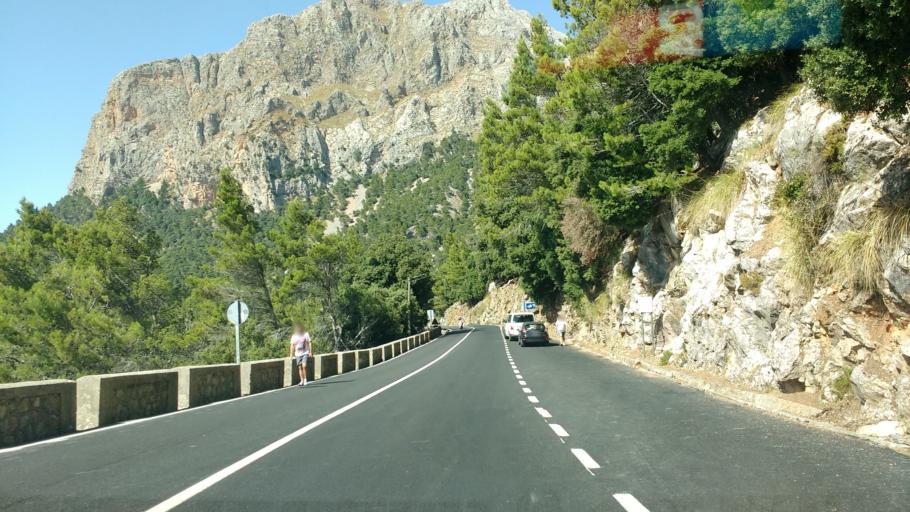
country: ES
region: Balearic Islands
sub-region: Illes Balears
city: Fornalutx
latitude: 39.7904
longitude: 2.7745
